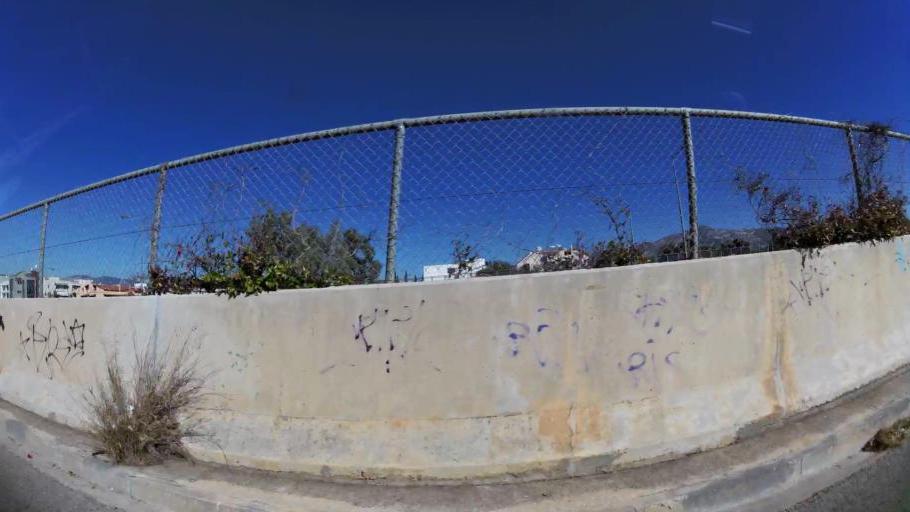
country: GR
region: Attica
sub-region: Nomarchia Athinas
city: Vrilissia
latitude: 38.0384
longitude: 23.8145
